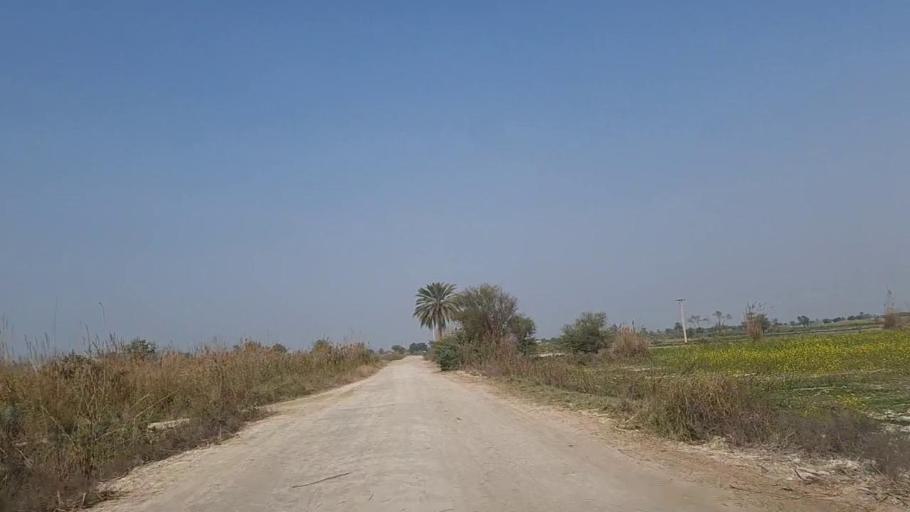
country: PK
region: Sindh
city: Daur
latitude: 26.4839
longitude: 68.4513
